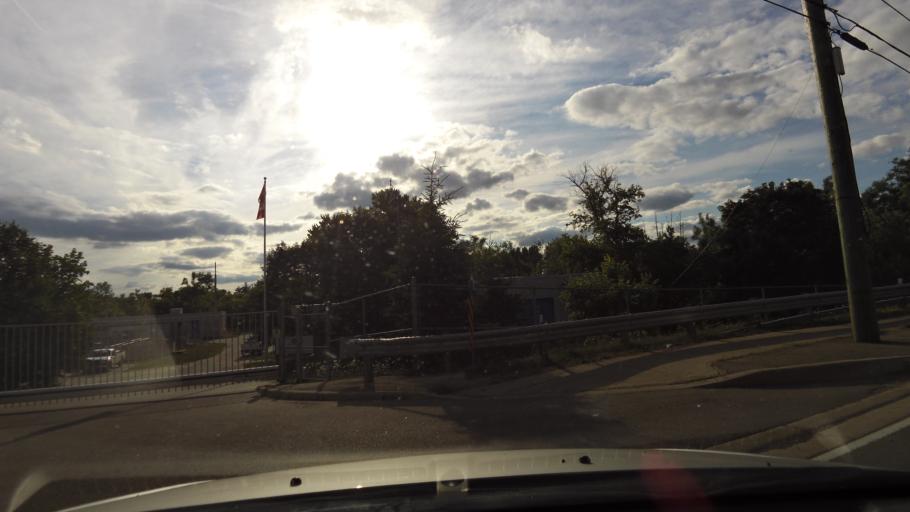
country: CA
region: Ontario
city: Angus
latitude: 44.1605
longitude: -79.8443
